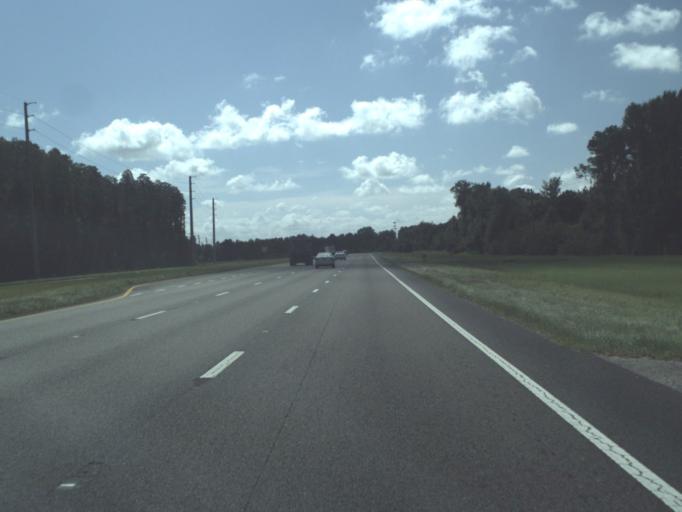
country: US
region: Florida
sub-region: Pasco County
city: Odessa
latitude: 28.1871
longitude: -82.5645
